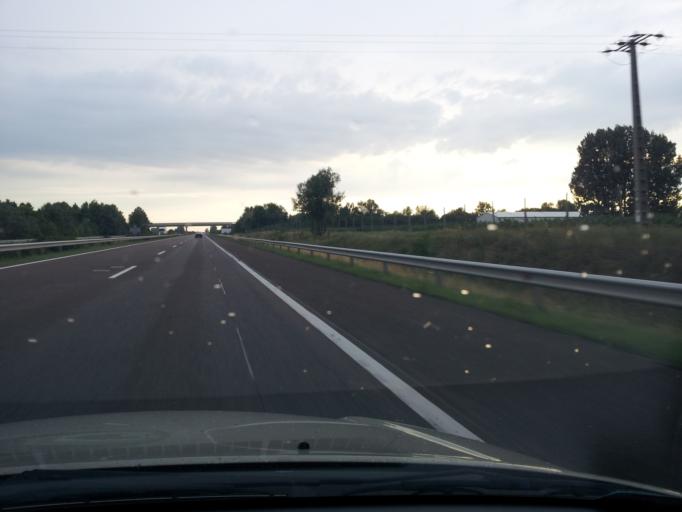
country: HU
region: Heves
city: Kal
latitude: 47.7166
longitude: 20.2612
